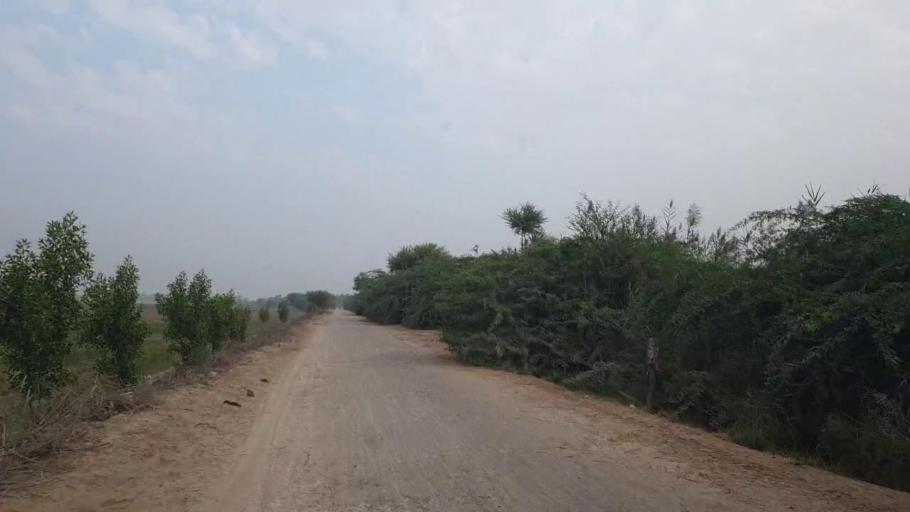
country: PK
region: Sindh
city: Talhar
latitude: 24.8285
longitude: 68.8801
